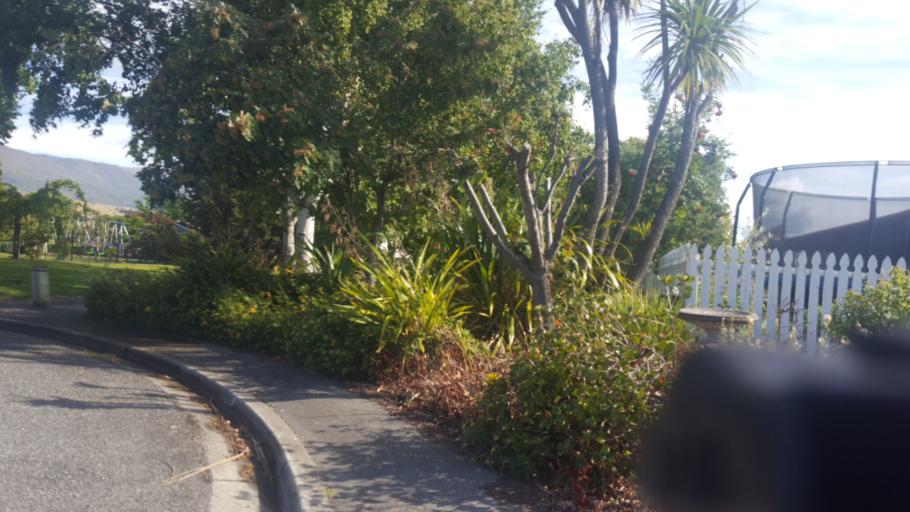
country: NZ
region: Otago
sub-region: Queenstown-Lakes District
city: Wanaka
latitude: -45.0459
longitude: 169.1981
